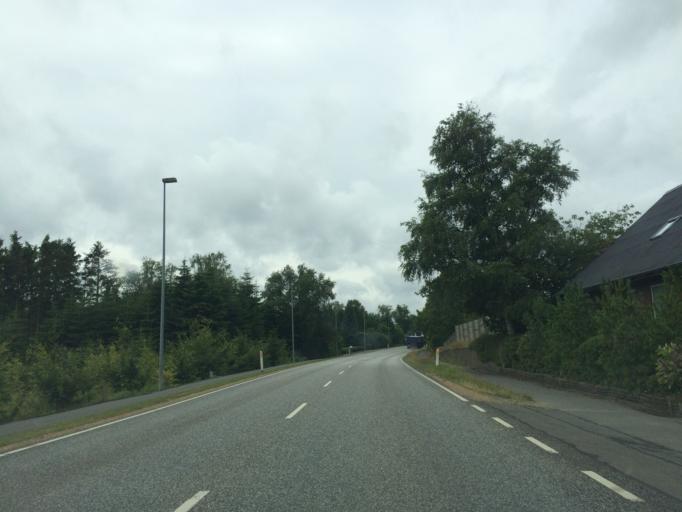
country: DK
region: Central Jutland
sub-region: Silkeborg Kommune
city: Silkeborg
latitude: 56.2011
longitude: 9.5973
